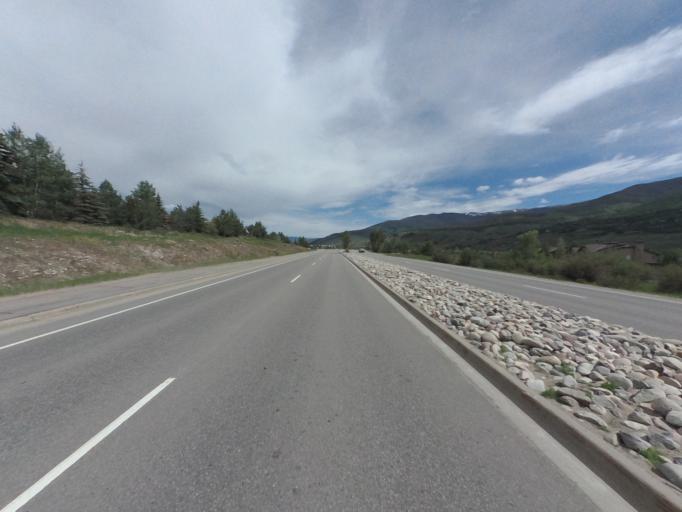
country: US
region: Colorado
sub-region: Summit County
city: Silverthorne
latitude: 39.6536
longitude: -106.0810
